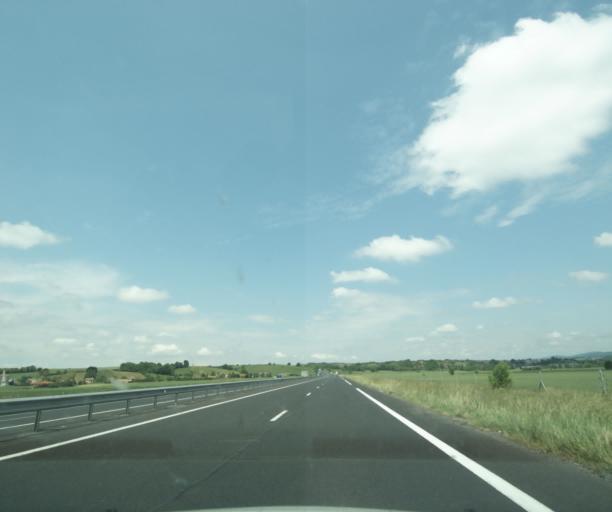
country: FR
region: Auvergne
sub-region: Departement de la Haute-Loire
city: Lempdes-sur-Allagnon
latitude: 45.4007
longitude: 3.2733
